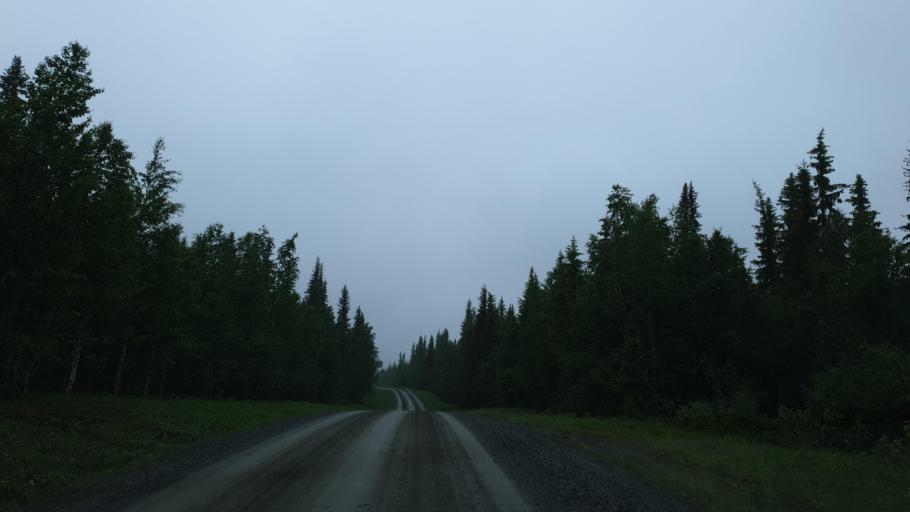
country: SE
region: Vaesterbotten
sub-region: Vilhelmina Kommun
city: Sjoberg
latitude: 65.2661
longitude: 15.9360
